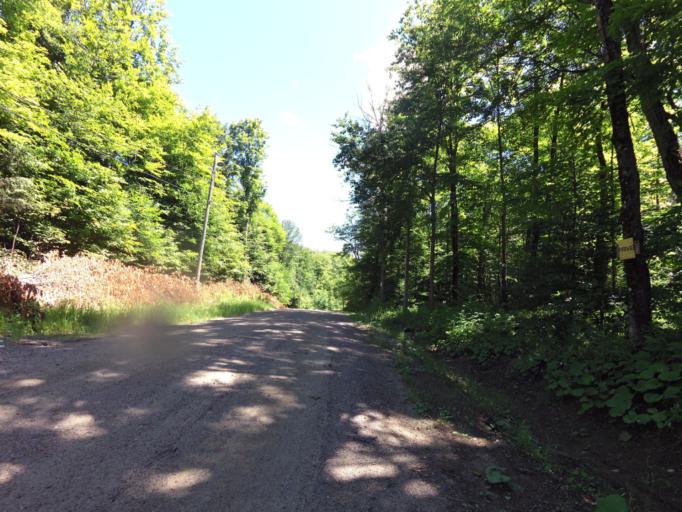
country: CA
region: Quebec
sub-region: Laurentides
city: Brownsburg-Chatham
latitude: 45.8332
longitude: -74.4893
